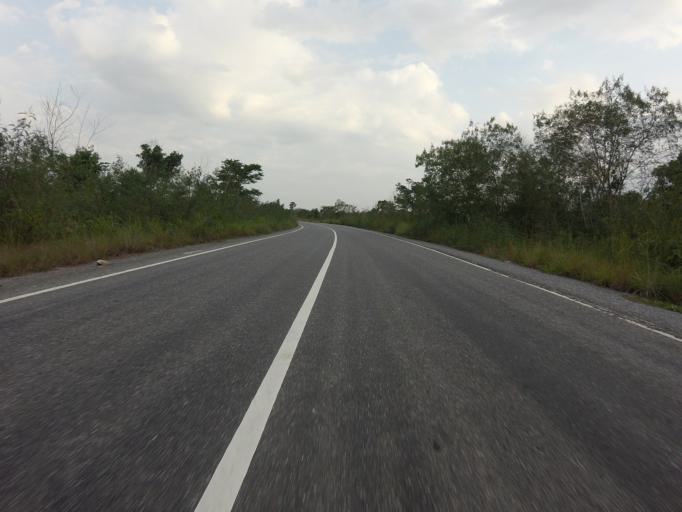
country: GH
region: Volta
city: Ho
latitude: 6.3441
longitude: 0.5386
